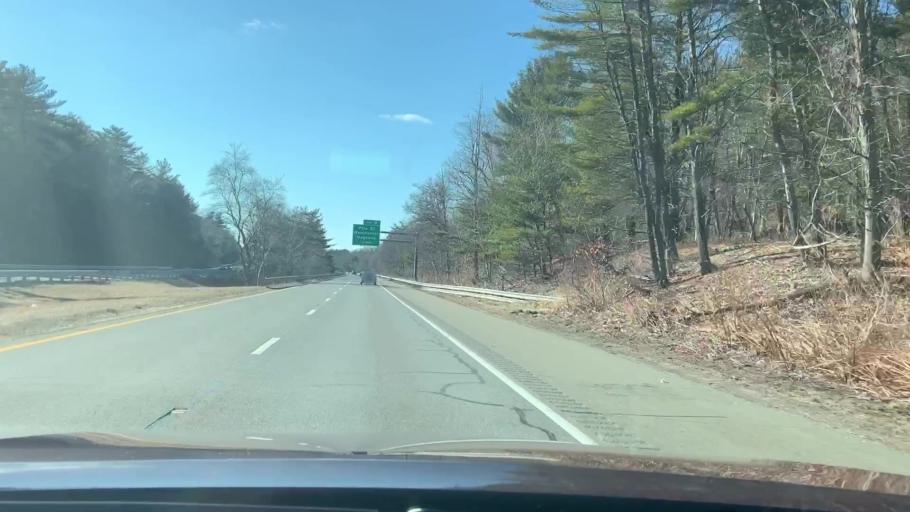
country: US
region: Massachusetts
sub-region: Essex County
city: Essex
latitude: 42.5916
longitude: -70.7773
